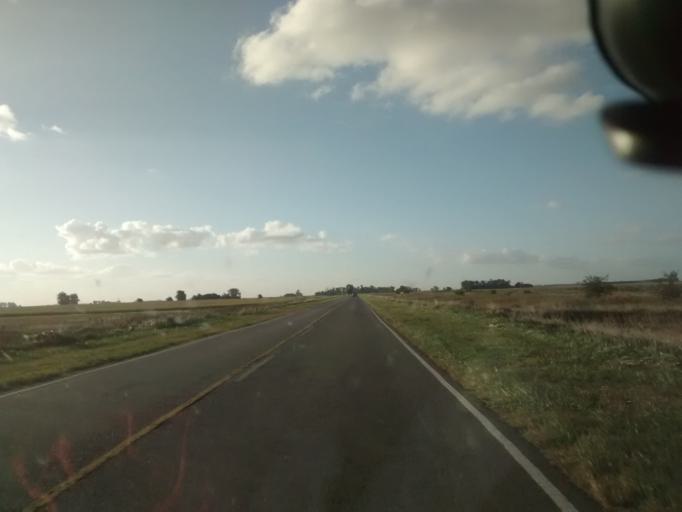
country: AR
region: Buenos Aires
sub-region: Partido de General Belgrano
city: General Belgrano
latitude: -36.1229
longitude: -58.5945
